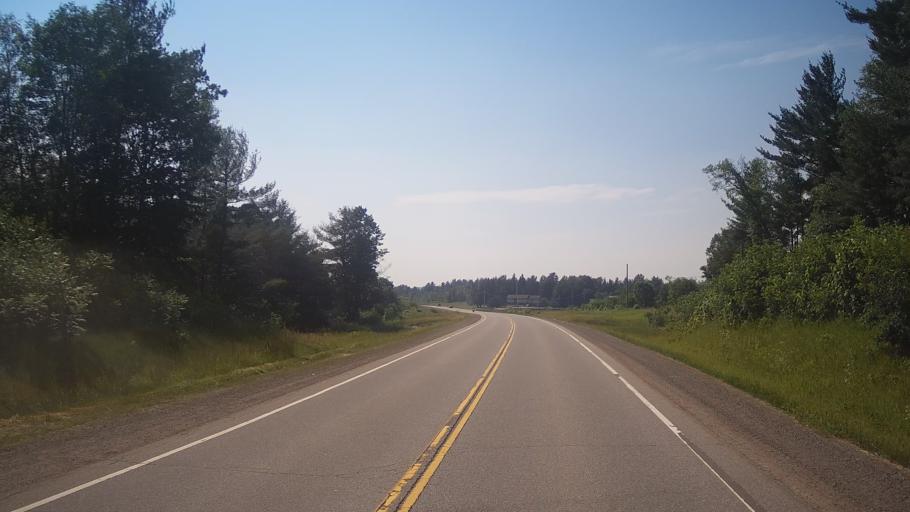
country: CA
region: Ontario
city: Pembroke
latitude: 45.5860
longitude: -77.2579
